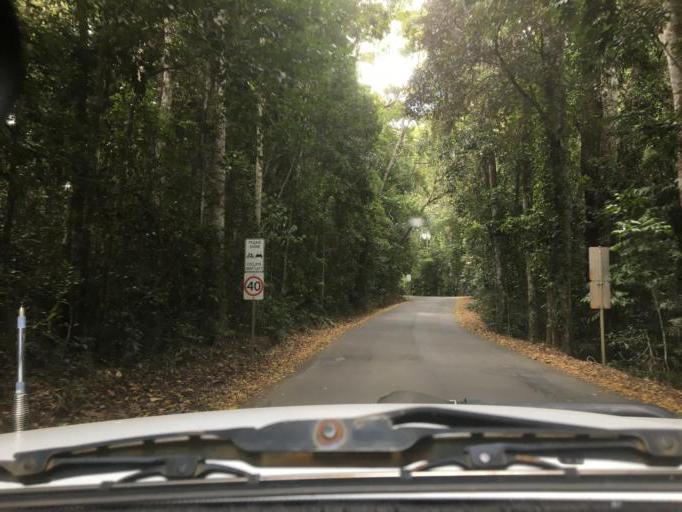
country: AU
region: Queensland
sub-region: Tablelands
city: Tolga
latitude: -17.2848
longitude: 145.6295
